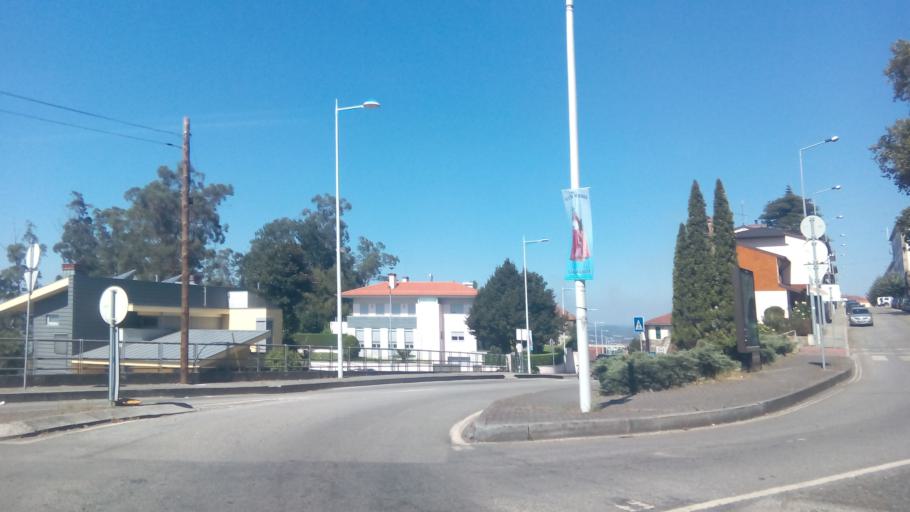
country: PT
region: Porto
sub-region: Penafiel
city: Penafiel
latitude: 41.2026
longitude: -8.2899
